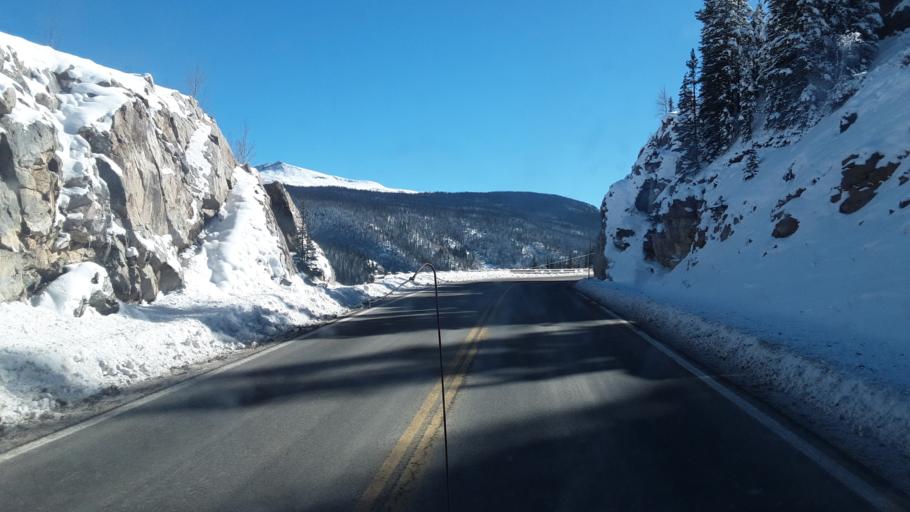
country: US
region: Colorado
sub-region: San Juan County
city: Silverton
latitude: 37.7873
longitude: -107.6724
